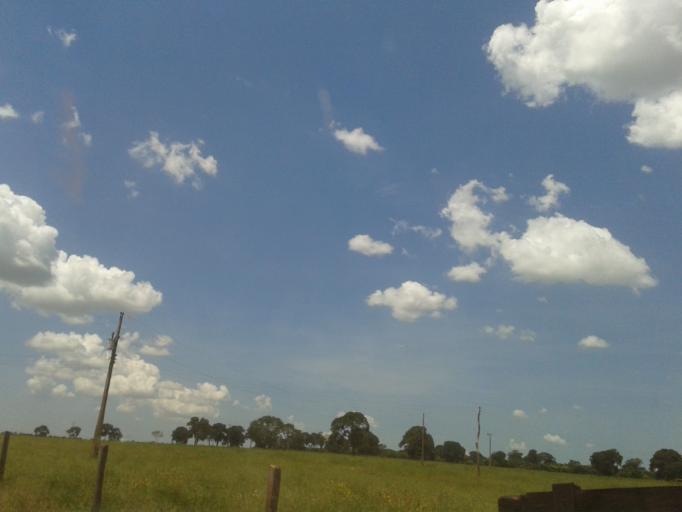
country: BR
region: Minas Gerais
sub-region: Santa Vitoria
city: Santa Vitoria
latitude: -19.2108
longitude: -50.4011
